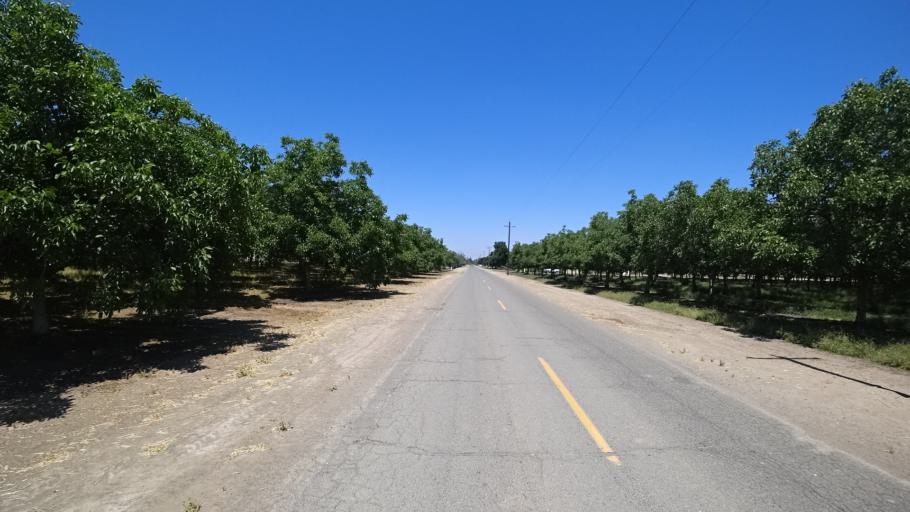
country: US
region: California
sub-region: Kings County
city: Lucerne
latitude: 36.4238
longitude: -119.6010
